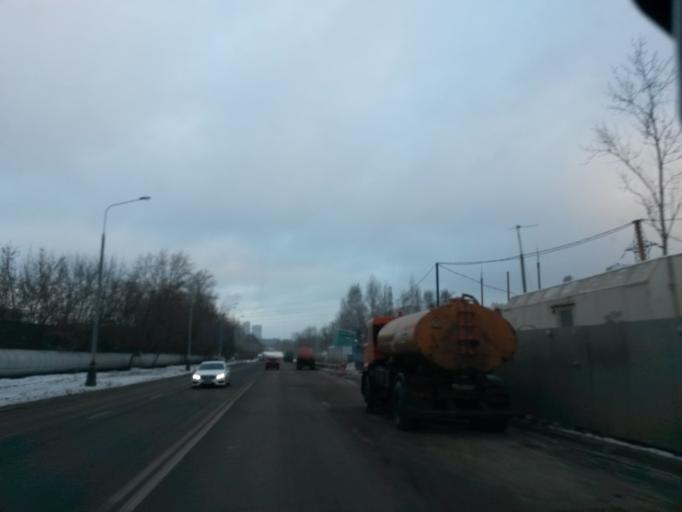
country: RU
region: Moscow
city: Amin'yevo
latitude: 55.6992
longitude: 37.4520
